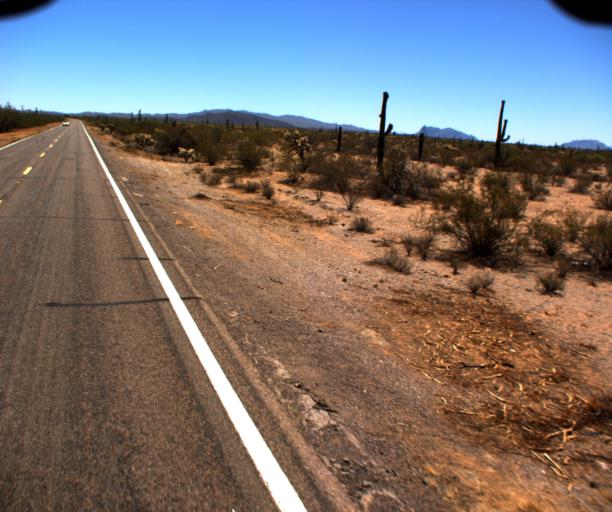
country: US
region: Arizona
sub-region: Pima County
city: Sells
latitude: 32.1814
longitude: -112.3268
